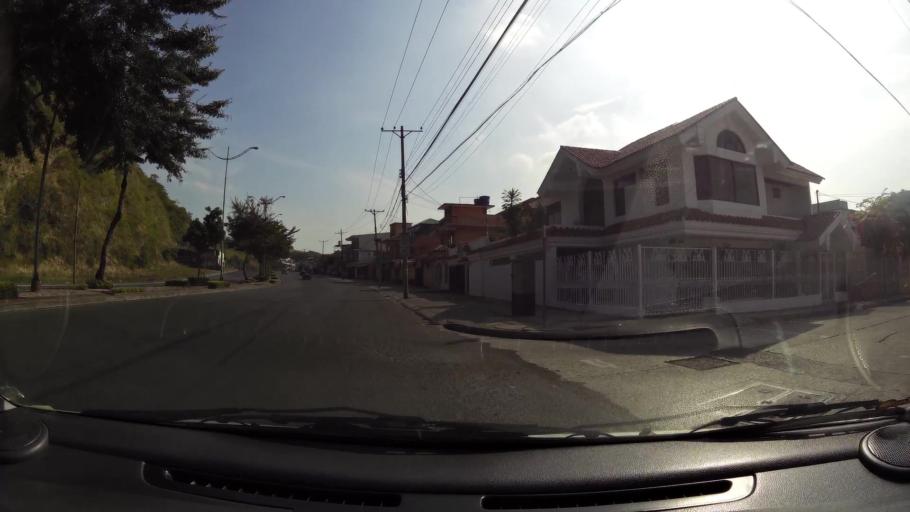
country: EC
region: Guayas
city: Guayaquil
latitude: -2.1857
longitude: -79.9120
